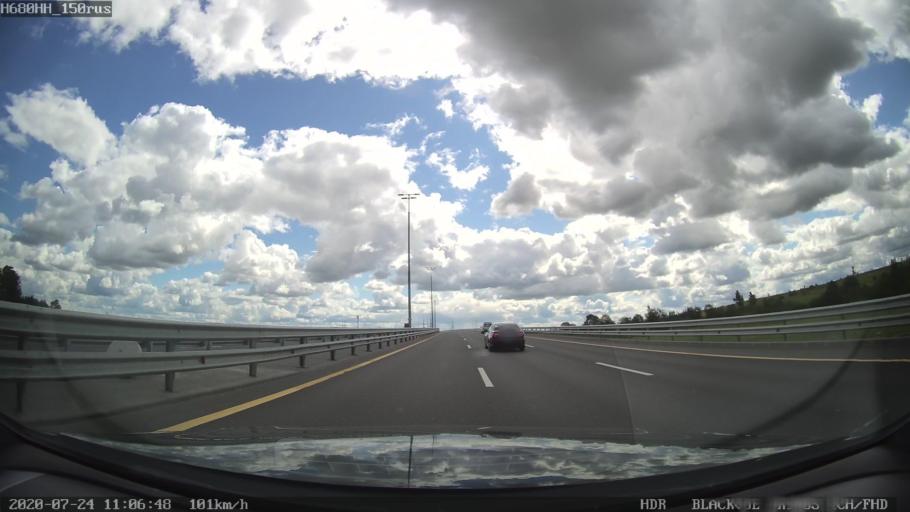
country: RU
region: St.-Petersburg
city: Pushkin
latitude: 59.7599
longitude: 30.3837
